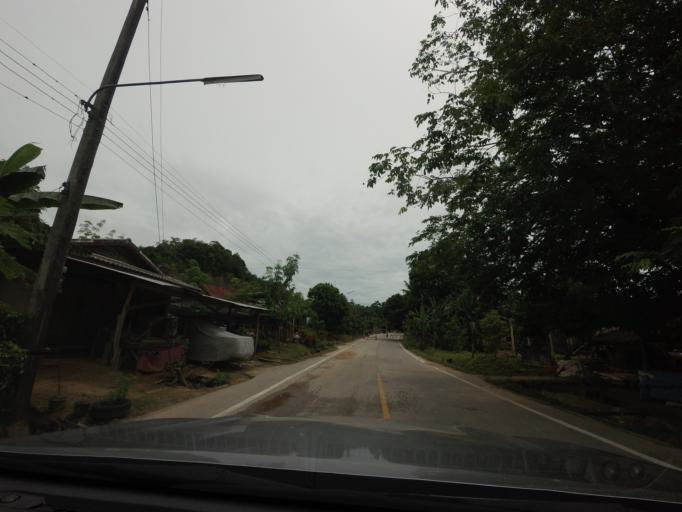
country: TH
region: Pattani
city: Sai Buri
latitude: 6.6630
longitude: 101.5511
